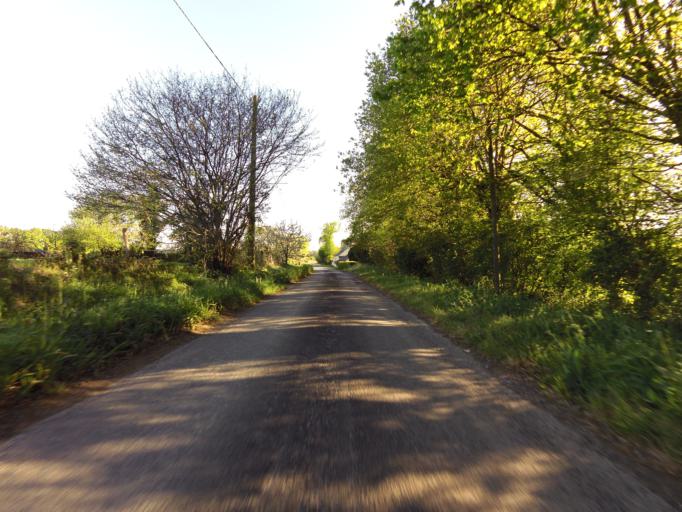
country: FR
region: Brittany
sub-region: Departement du Morbihan
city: Pluherlin
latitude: 47.7216
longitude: -2.3566
